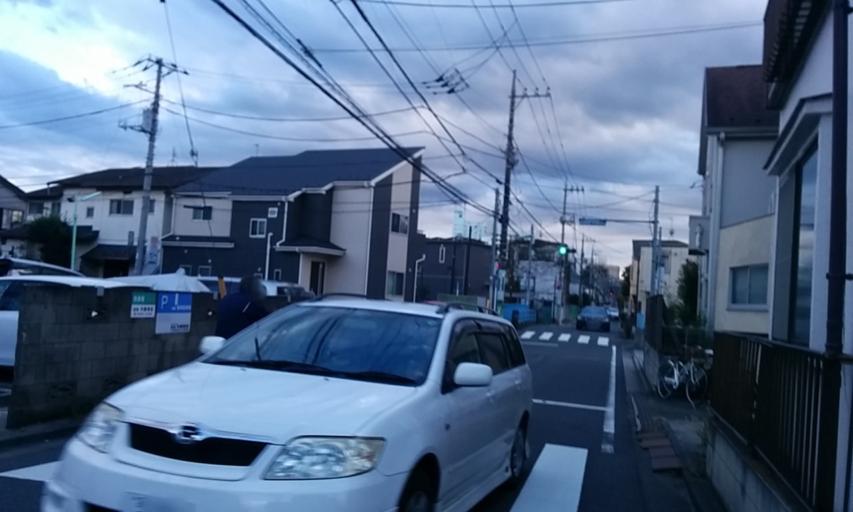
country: JP
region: Tokyo
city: Tokyo
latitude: 35.6731
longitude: 139.6369
